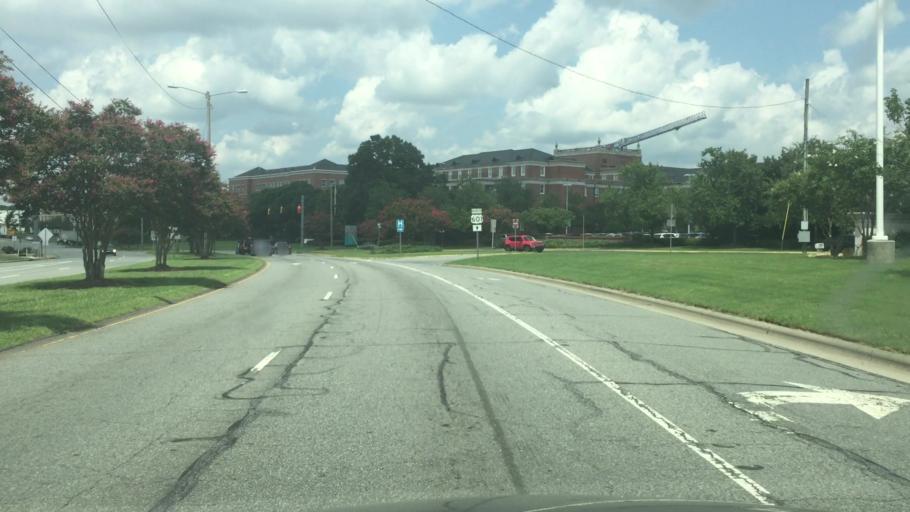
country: US
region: North Carolina
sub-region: Cabarrus County
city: Concord
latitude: 35.4339
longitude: -80.6037
